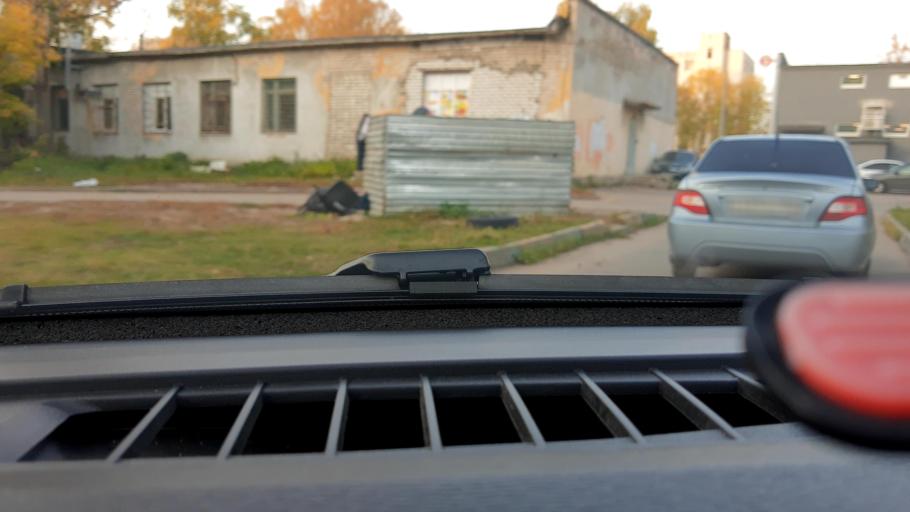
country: RU
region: Nizjnij Novgorod
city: Gorbatovka
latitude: 56.3451
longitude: 43.8034
